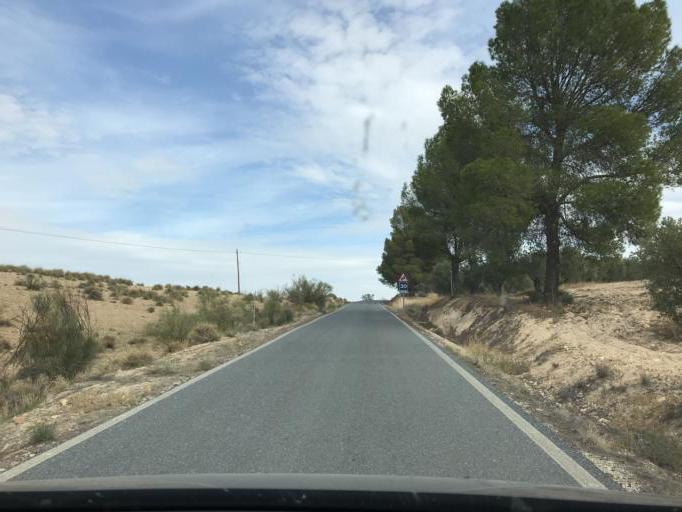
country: ES
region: Andalusia
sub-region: Provincia de Granada
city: Villanueva de las Torres
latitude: 37.5097
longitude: -3.1041
